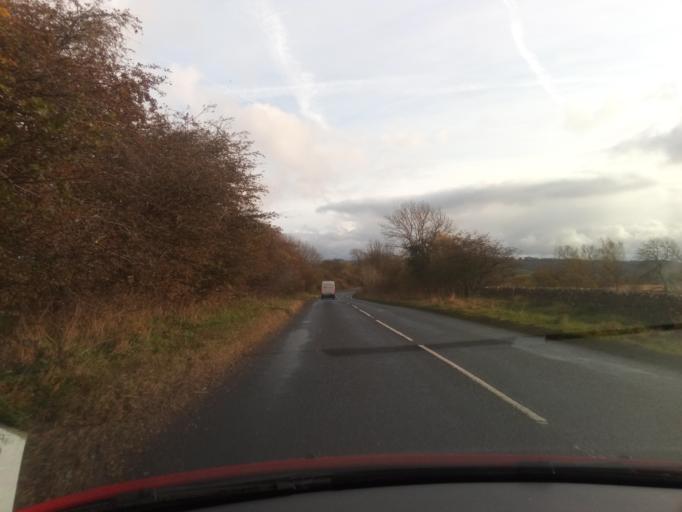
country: GB
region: England
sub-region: Northumberland
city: Wall
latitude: 55.0417
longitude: -2.1439
